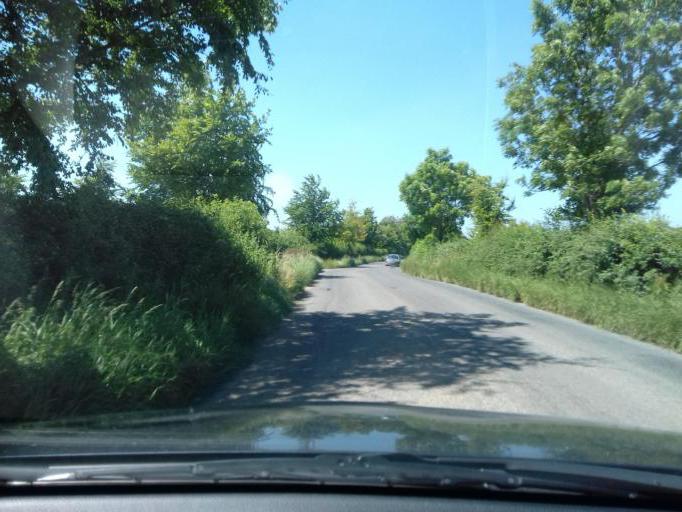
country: IE
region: Leinster
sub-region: Fingal County
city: Swords
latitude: 53.5252
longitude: -6.2945
